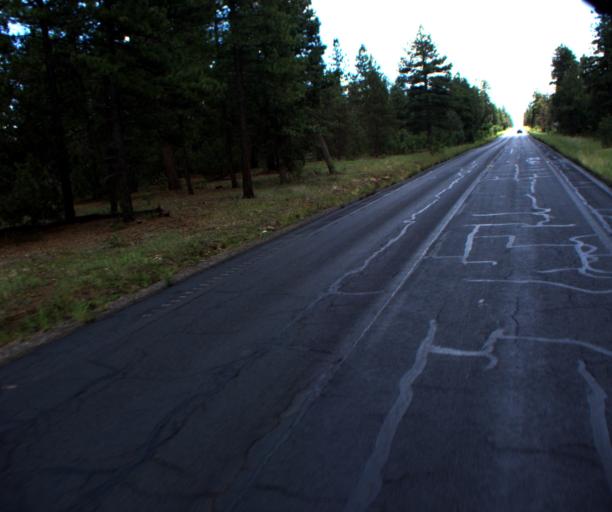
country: US
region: Arizona
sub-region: Gila County
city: Pine
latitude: 34.4971
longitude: -111.4599
